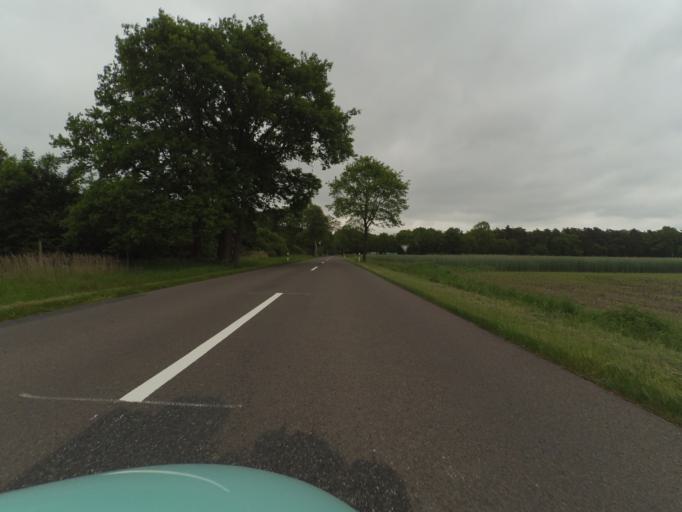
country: DE
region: Lower Saxony
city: Adenbuettel
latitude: 52.3948
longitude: 10.4501
